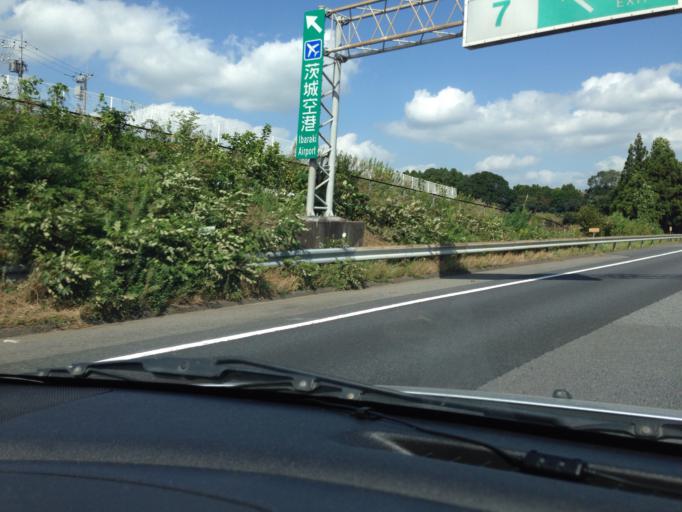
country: JP
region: Ibaraki
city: Ishioka
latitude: 36.1701
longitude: 140.2413
